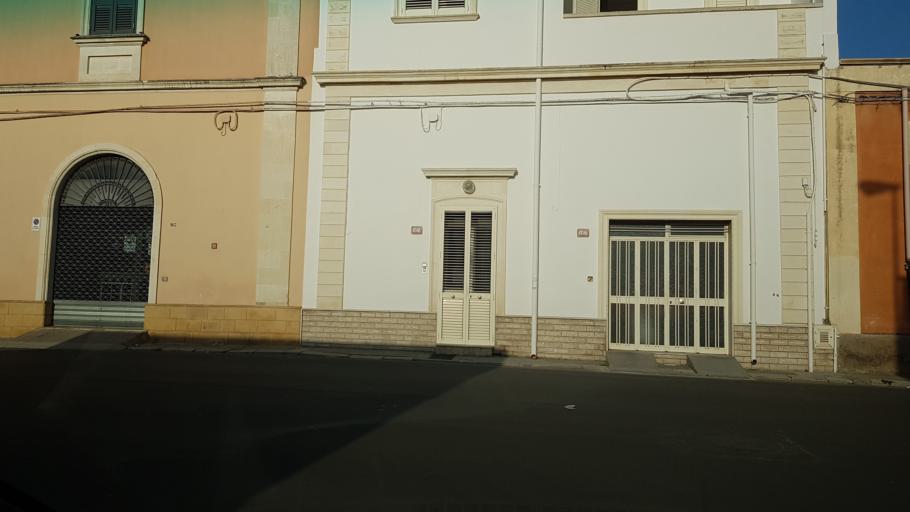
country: IT
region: Apulia
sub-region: Provincia di Lecce
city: Squinzano
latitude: 40.4329
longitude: 18.0487
